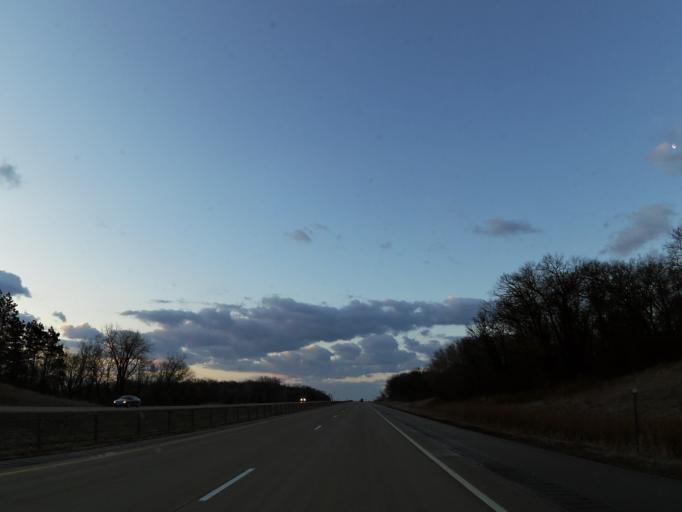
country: US
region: Minnesota
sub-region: Scott County
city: Elko New Market
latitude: 44.5304
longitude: -93.2995
